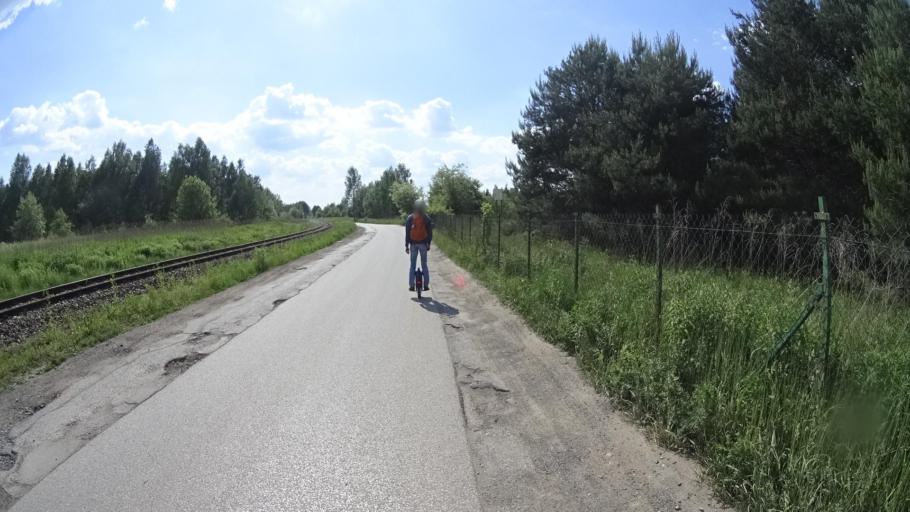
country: PL
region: Masovian Voivodeship
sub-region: Powiat piaseczynski
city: Jozefoslaw
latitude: 52.0965
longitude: 21.0763
